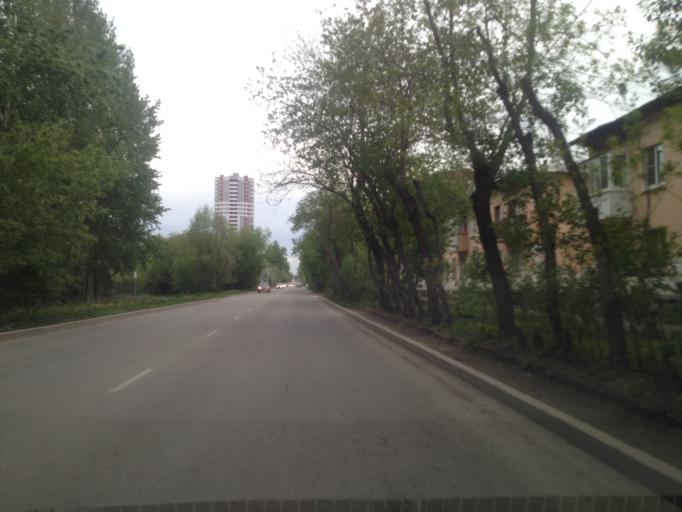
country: RU
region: Sverdlovsk
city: Sovkhoznyy
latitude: 56.7702
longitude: 60.6017
